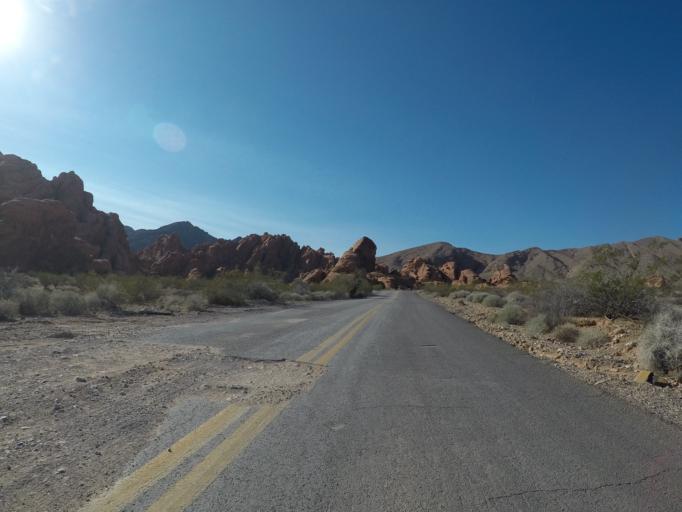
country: US
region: Nevada
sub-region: Clark County
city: Moapa Valley
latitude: 36.4207
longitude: -114.5560
